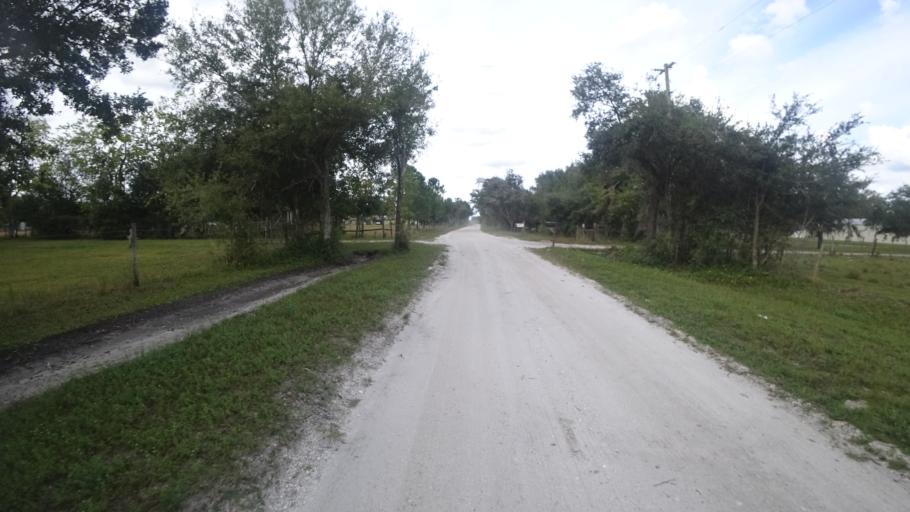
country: US
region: Florida
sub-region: Sarasota County
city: Lake Sarasota
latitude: 27.3973
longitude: -82.2664
